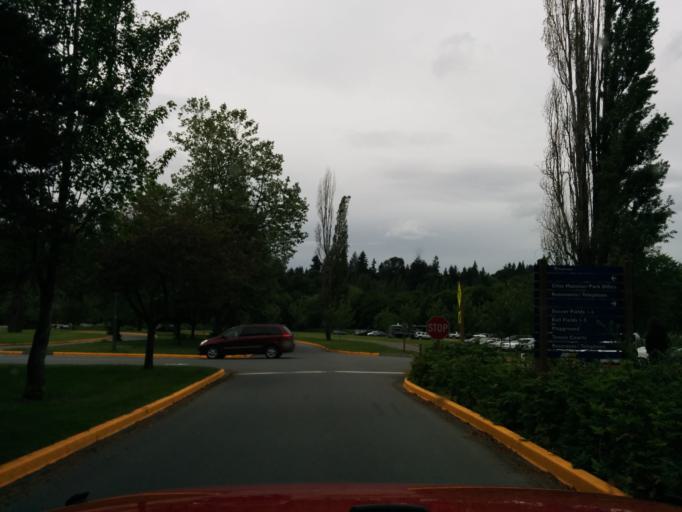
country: US
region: Washington
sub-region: King County
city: Redmond
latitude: 47.6640
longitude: -122.1210
